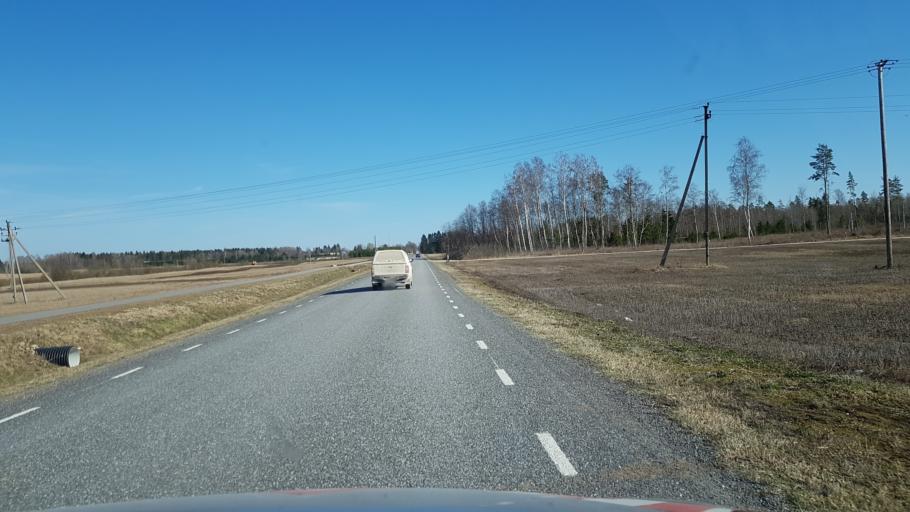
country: EE
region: Laeaene-Virumaa
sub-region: Rakke vald
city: Rakke
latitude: 58.9976
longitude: 26.2091
